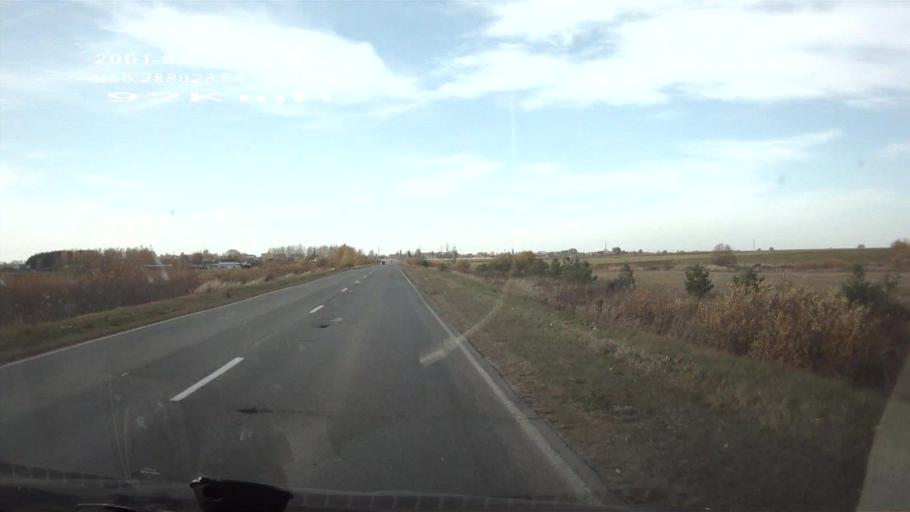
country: RU
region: Chuvashia
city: Ibresi
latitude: 55.2881
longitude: 47.0717
